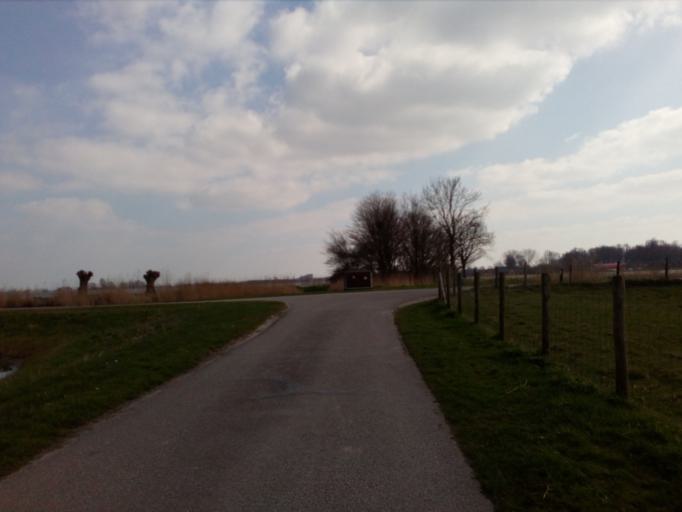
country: NL
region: South Holland
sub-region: Gemeente Zoetermeer
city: Zoetermeer
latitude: 52.0830
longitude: 4.5004
